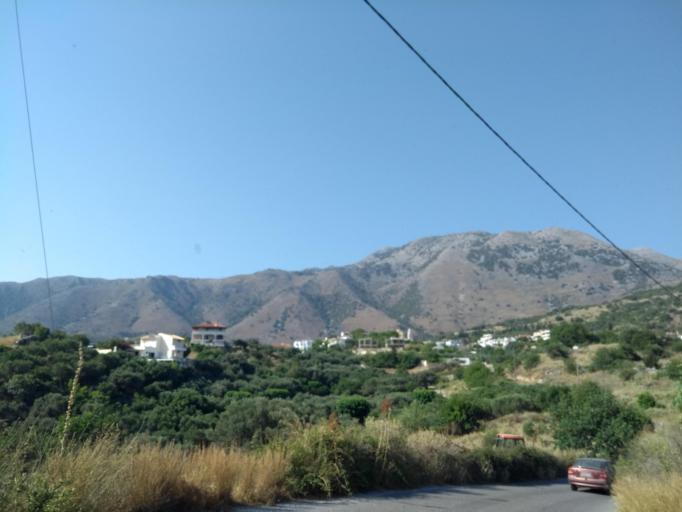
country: GR
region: Crete
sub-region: Nomos Chanias
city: Georgioupolis
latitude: 35.3191
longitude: 24.2971
